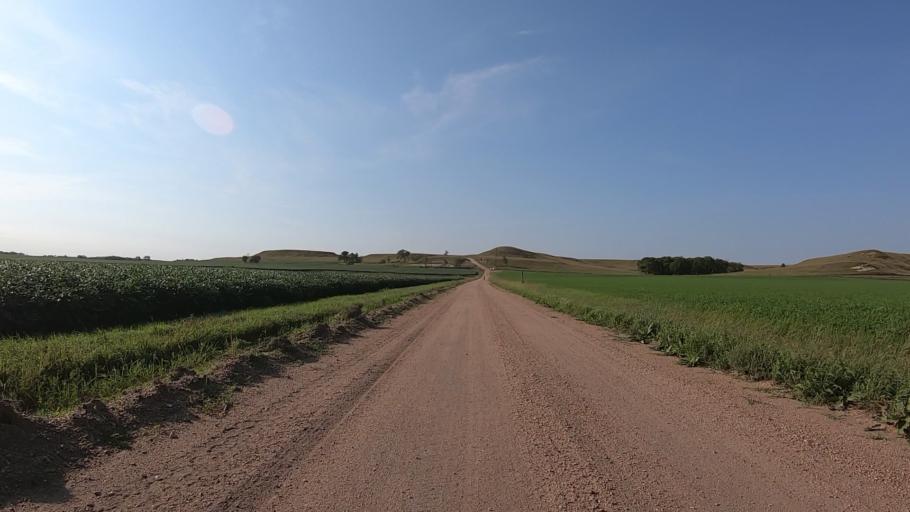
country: US
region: Kansas
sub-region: Marshall County
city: Blue Rapids
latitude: 39.6542
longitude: -96.8815
